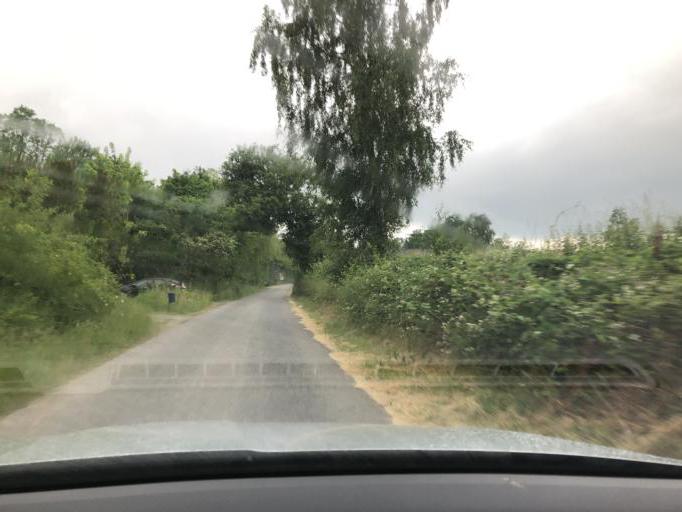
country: SE
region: Blekinge
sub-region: Solvesborgs Kommun
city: Soelvesborg
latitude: 56.1047
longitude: 14.6176
